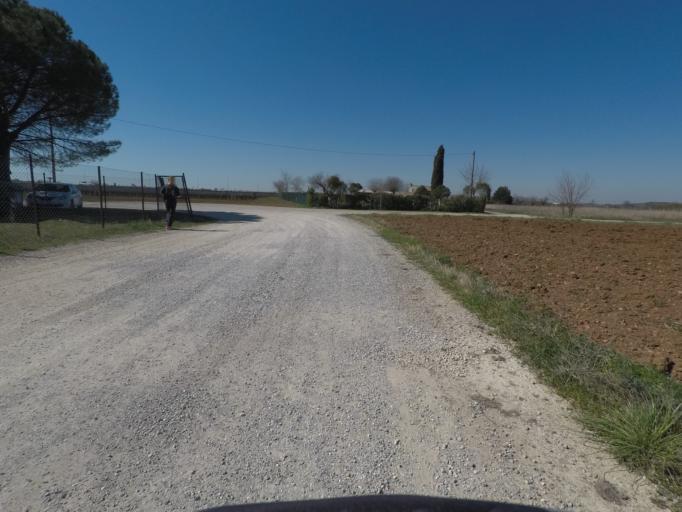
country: IT
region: Friuli Venezia Giulia
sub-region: Provincia di Gorizia
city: Gradisca d'Isonzo
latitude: 45.9013
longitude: 13.4845
